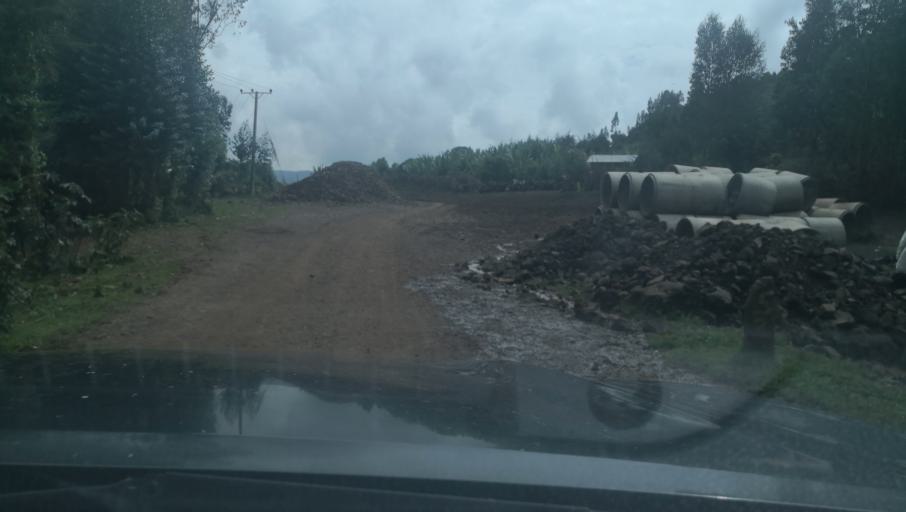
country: ET
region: Southern Nations, Nationalities, and People's Region
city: Butajira
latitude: 8.3289
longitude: 38.3640
